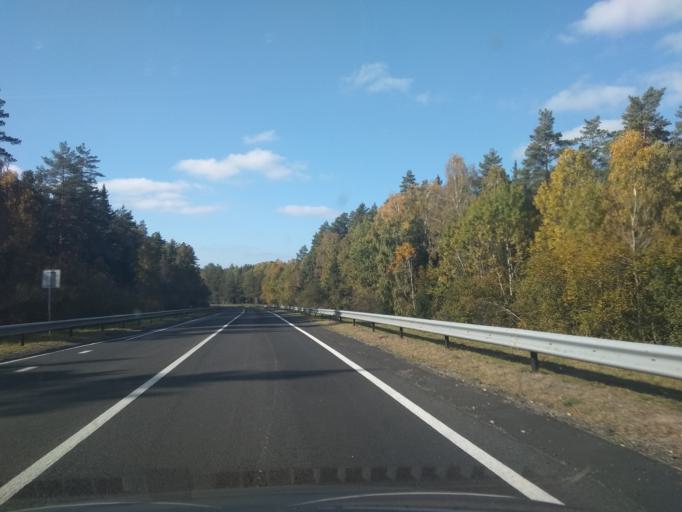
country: BY
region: Brest
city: Baranovichi
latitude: 53.0485
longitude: 25.8429
